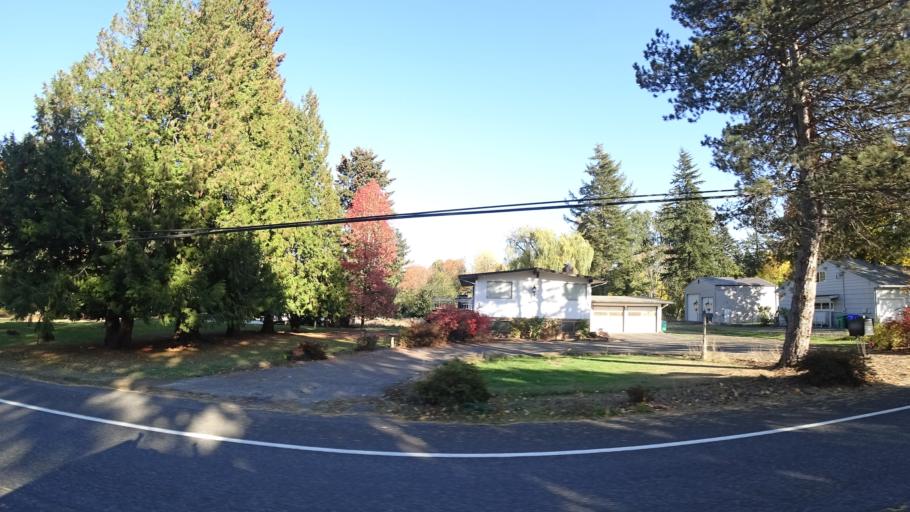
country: US
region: Oregon
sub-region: Multnomah County
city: Gresham
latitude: 45.4845
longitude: -122.4231
